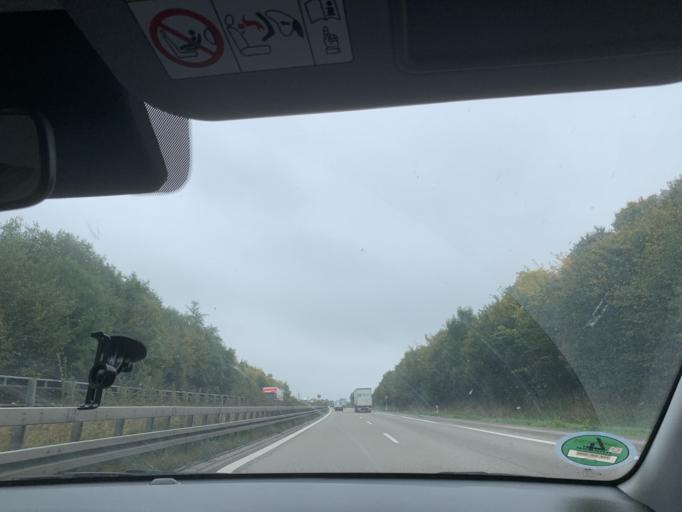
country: DE
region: Baden-Wuerttemberg
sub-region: Regierungsbezirk Stuttgart
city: Wallhausen
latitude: 49.1769
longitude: 10.0265
